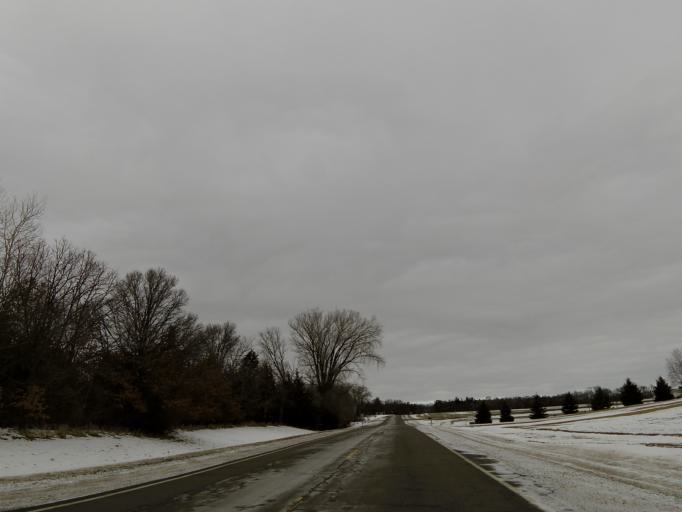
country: US
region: Minnesota
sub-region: Washington County
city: Cottage Grove
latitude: 44.8028
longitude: -92.8935
